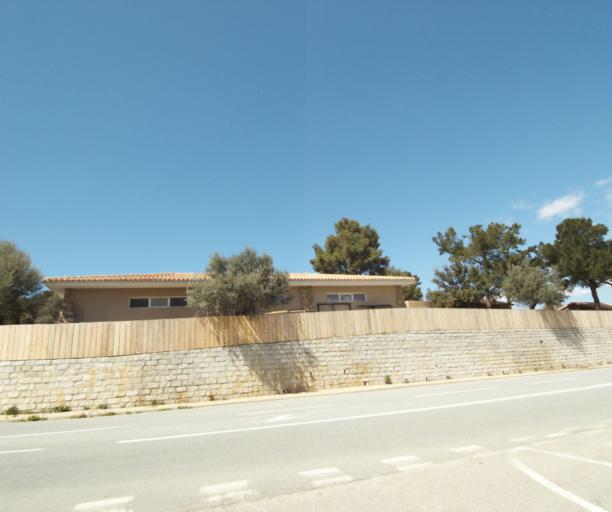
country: FR
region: Corsica
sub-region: Departement de la Corse-du-Sud
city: Propriano
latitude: 41.6438
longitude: 8.8688
